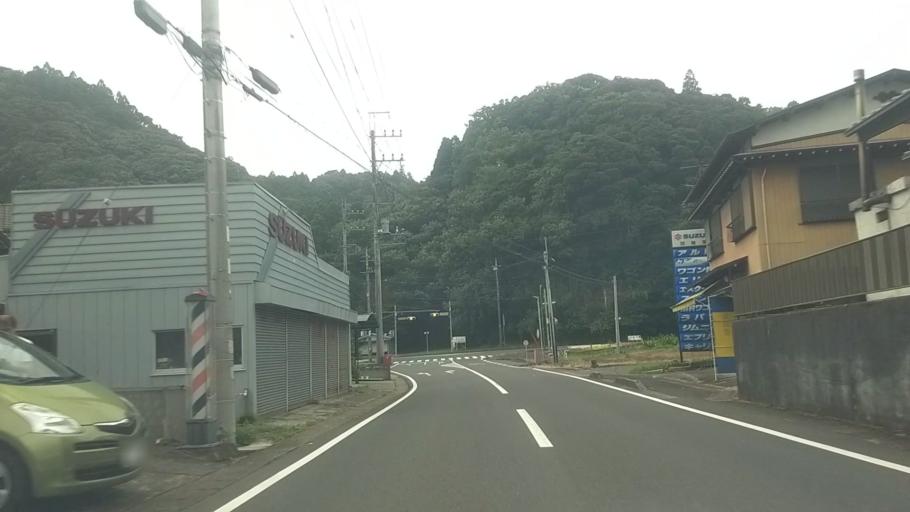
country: JP
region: Chiba
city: Ohara
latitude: 35.2703
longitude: 140.2549
